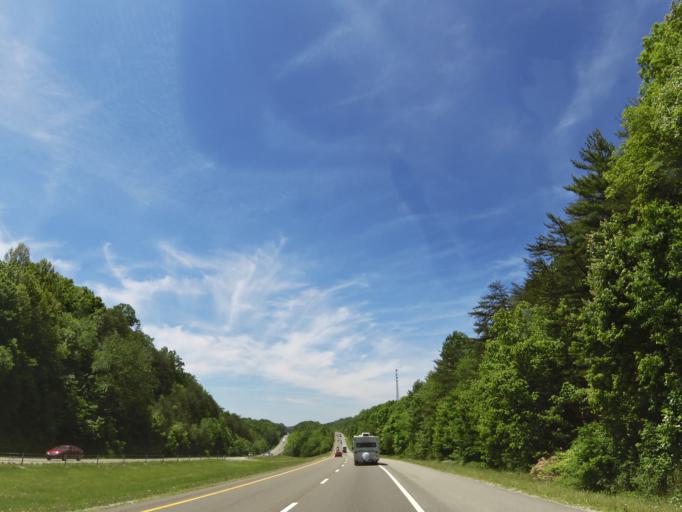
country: US
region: Tennessee
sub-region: Campbell County
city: Hunter
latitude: 36.4647
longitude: -84.2478
